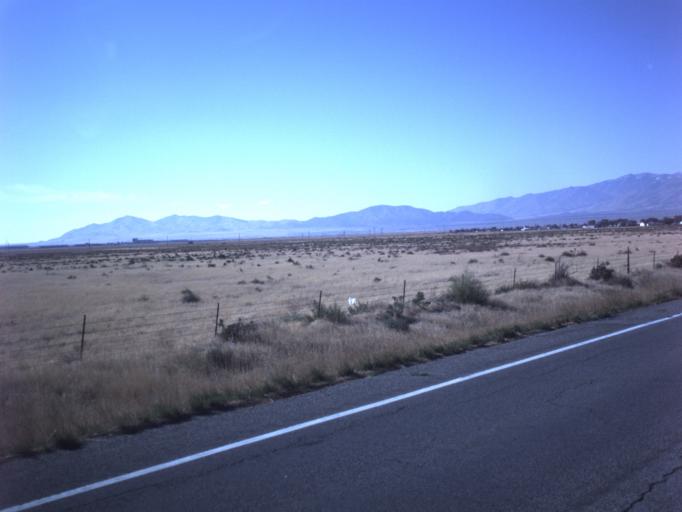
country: US
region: Utah
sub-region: Tooele County
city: Erda
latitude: 40.6094
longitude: -112.3808
